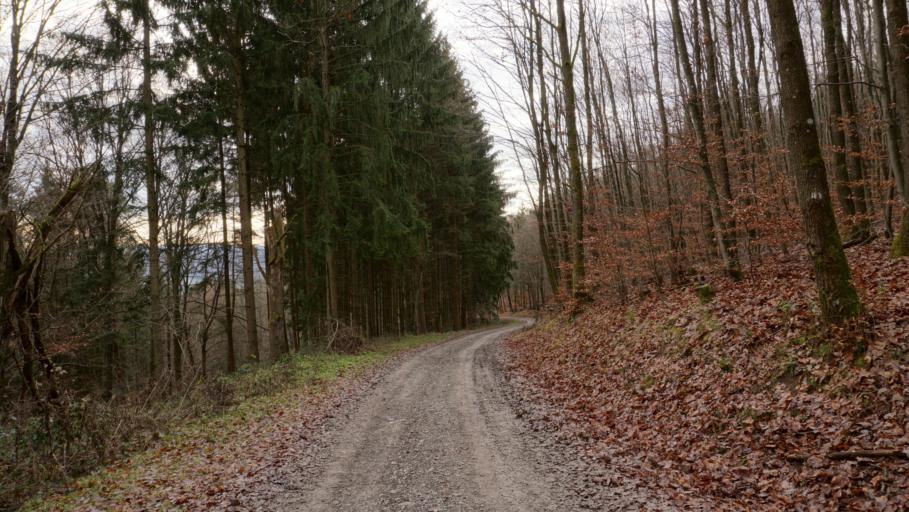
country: DE
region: Baden-Wuerttemberg
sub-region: Karlsruhe Region
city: Neckargerach
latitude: 49.4079
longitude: 9.0747
